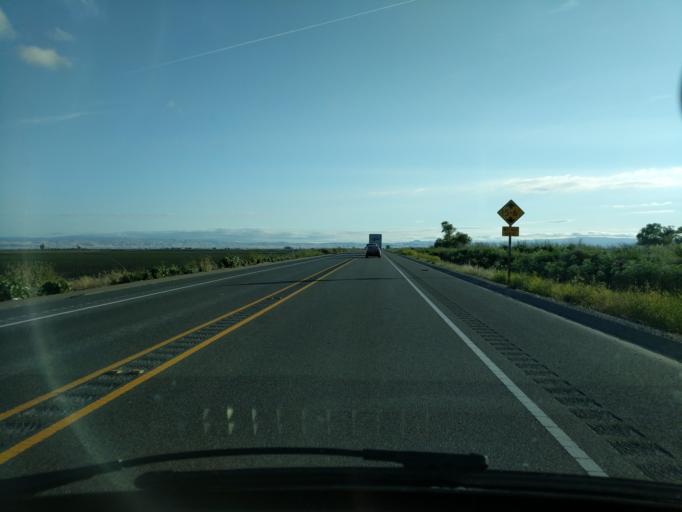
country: US
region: California
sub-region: San Joaquin County
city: Country Club
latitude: 37.9076
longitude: -121.4571
